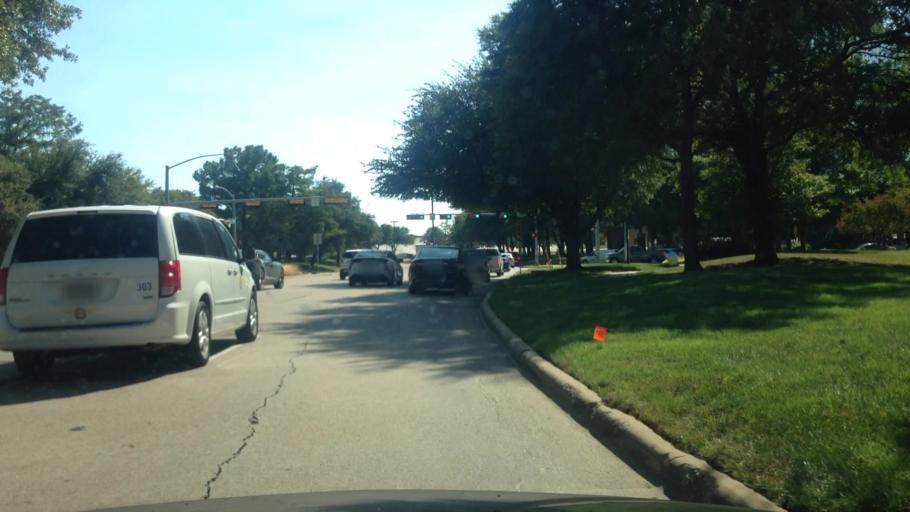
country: US
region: Texas
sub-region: Dallas County
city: Coppell
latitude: 32.9241
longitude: -97.0178
